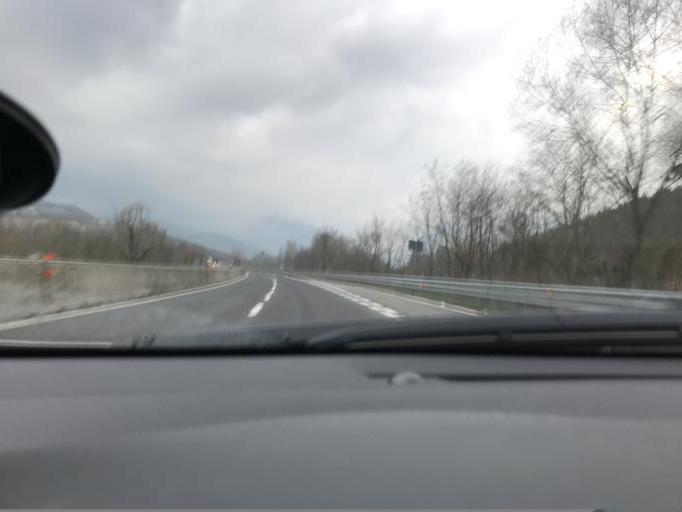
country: IT
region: The Marches
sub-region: Provincia di Ancona
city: Mergo
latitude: 43.4589
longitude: 13.0497
